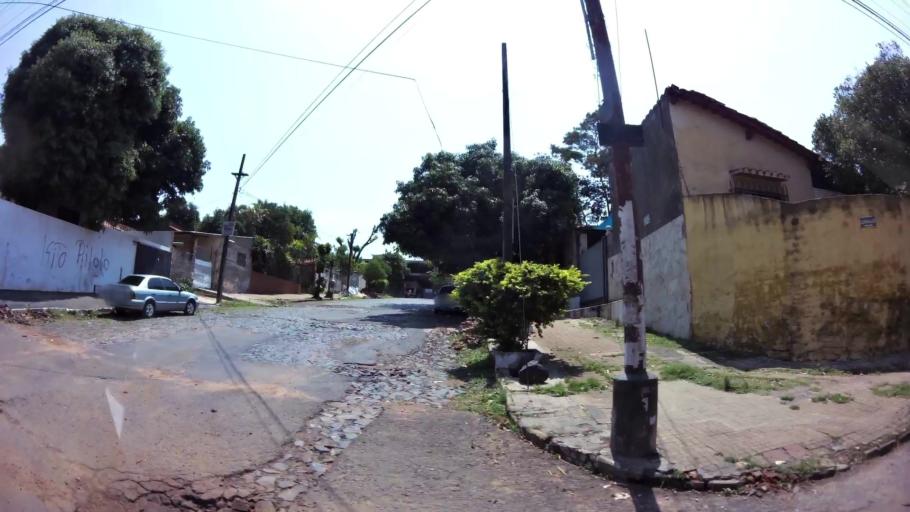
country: PY
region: Asuncion
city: Asuncion
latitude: -25.3009
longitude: -57.6392
